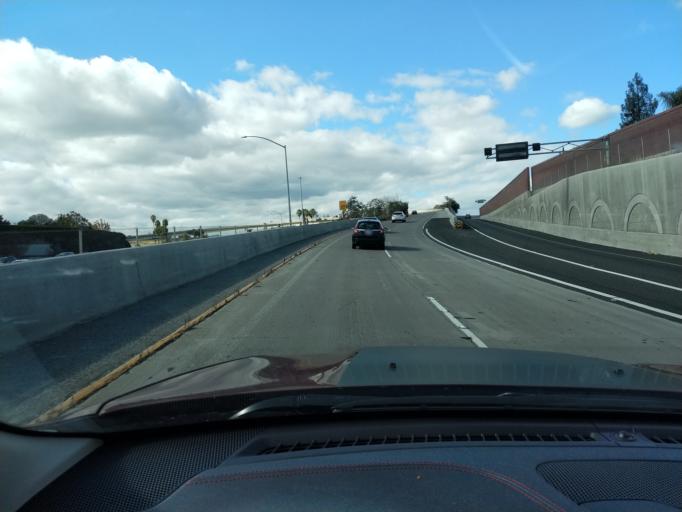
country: US
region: California
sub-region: Santa Clara County
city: Burbank
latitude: 37.3176
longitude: -121.9361
